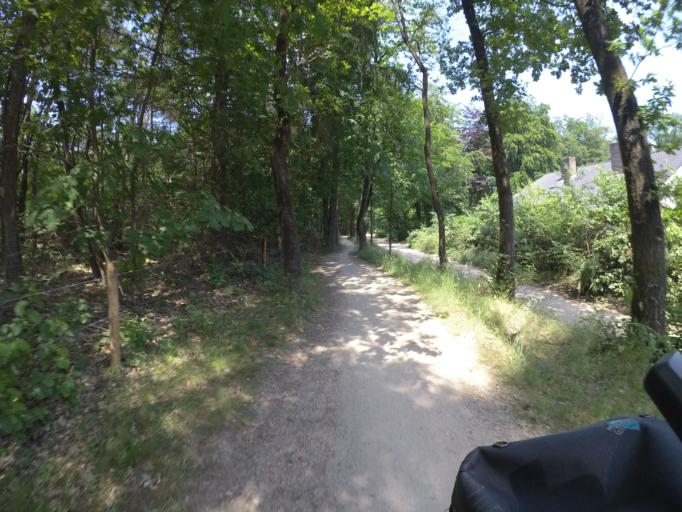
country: NL
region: Overijssel
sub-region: Gemeente Twenterand
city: Den Ham
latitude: 52.3598
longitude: 6.4465
